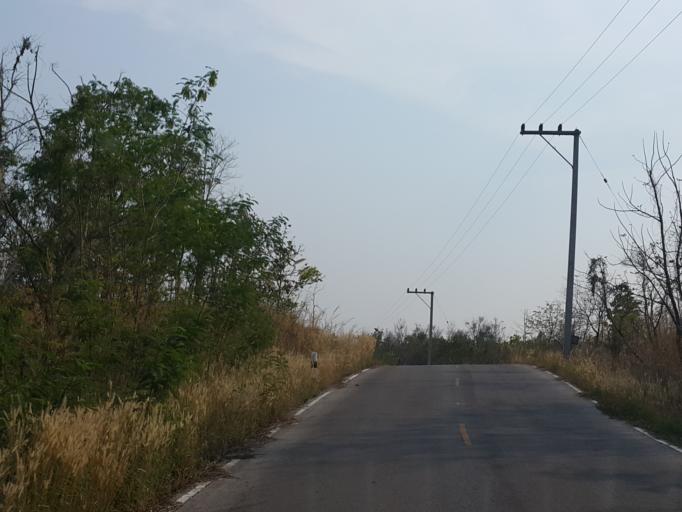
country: TH
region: Lampang
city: Chae Hom
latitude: 18.7334
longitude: 99.5465
